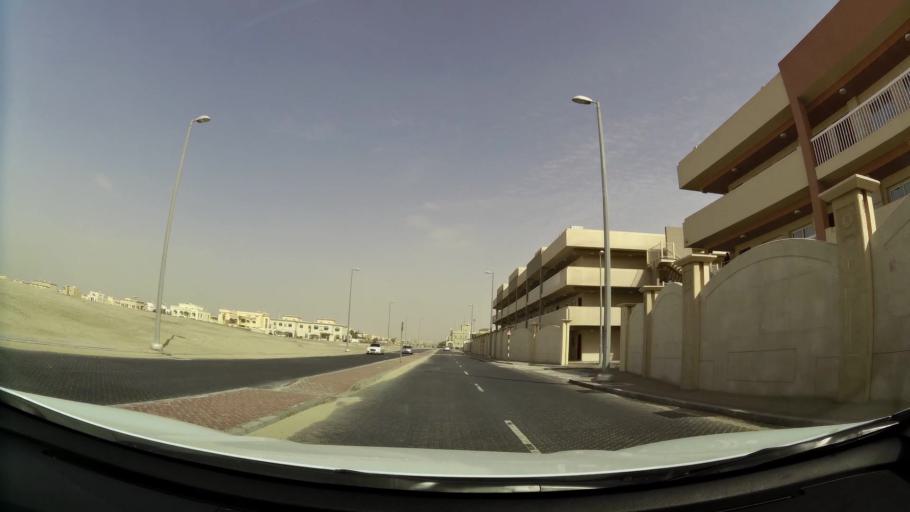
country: AE
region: Abu Dhabi
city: Abu Dhabi
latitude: 24.4133
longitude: 54.5470
